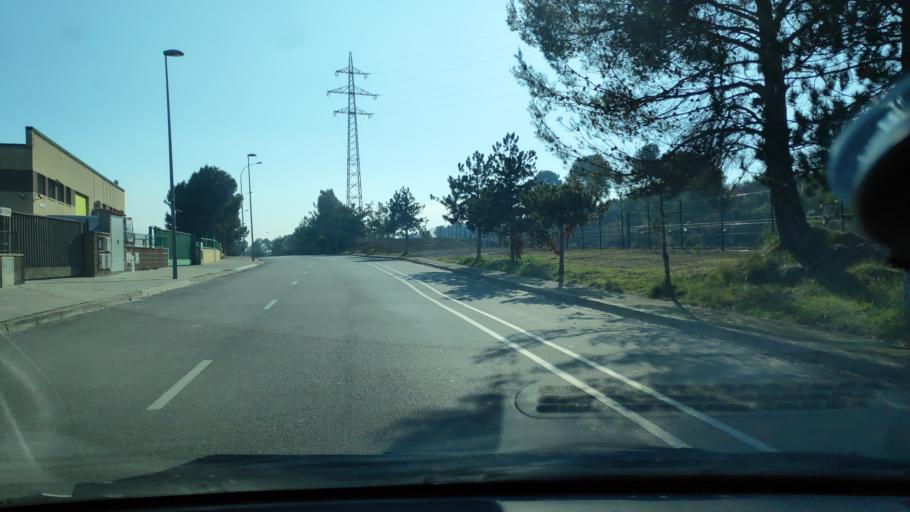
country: ES
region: Catalonia
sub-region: Provincia de Barcelona
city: Sant Quirze del Valles
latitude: 41.5225
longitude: 2.0898
